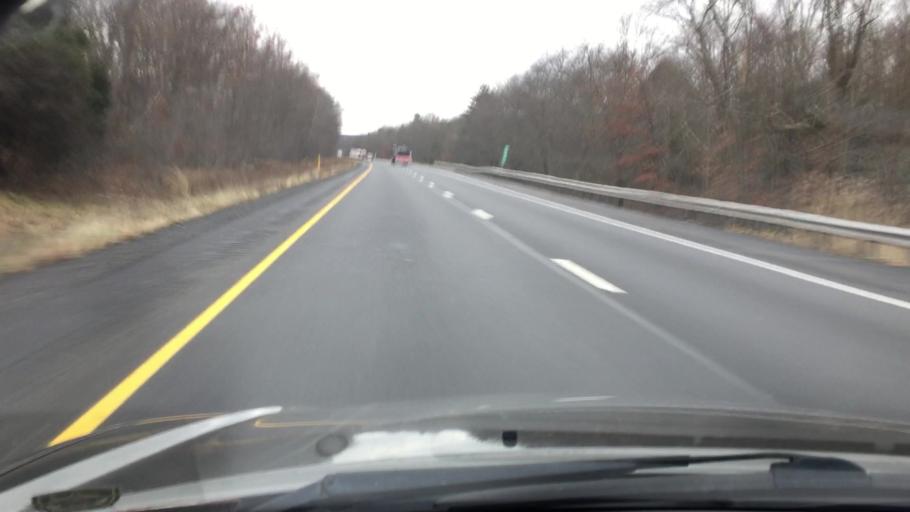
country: US
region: Pennsylvania
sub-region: Luzerne County
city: White Haven
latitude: 41.0559
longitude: -75.8282
